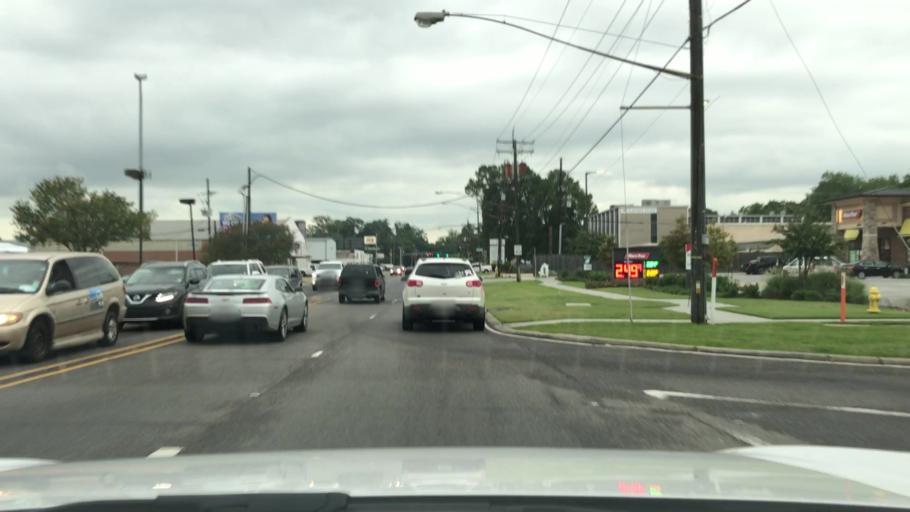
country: US
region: Louisiana
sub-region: East Baton Rouge Parish
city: Baton Rouge
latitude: 30.4509
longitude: -91.1390
